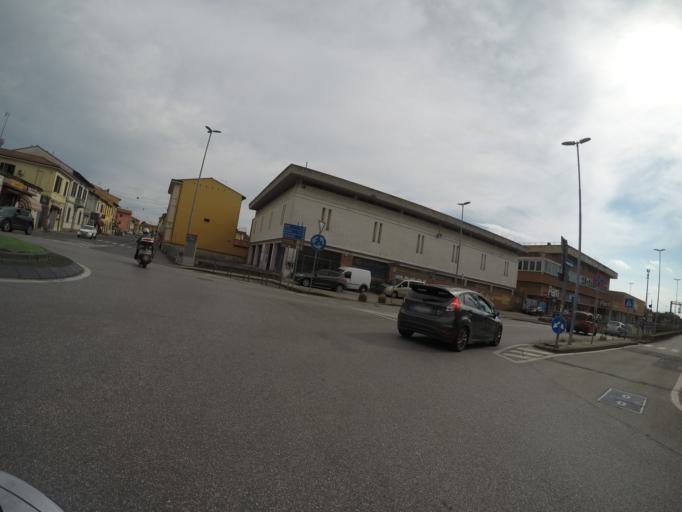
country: IT
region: Tuscany
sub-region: Province of Pisa
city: Pisa
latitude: 43.7250
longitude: 10.3911
